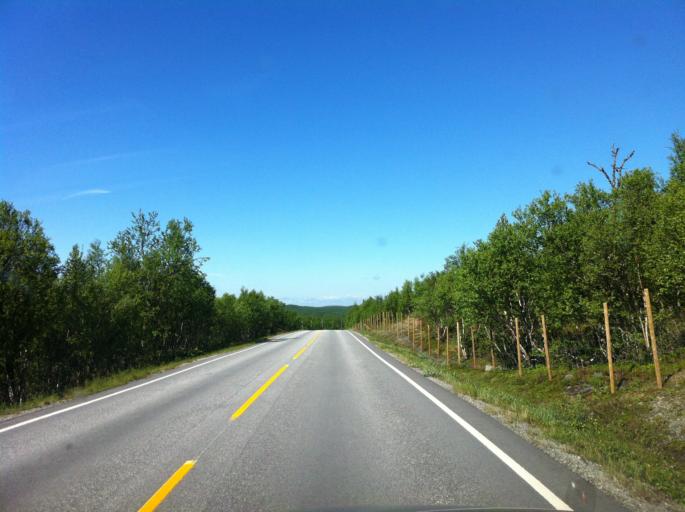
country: NO
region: Sor-Trondelag
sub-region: Tydal
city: Aas
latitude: 62.6359
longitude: 11.9419
